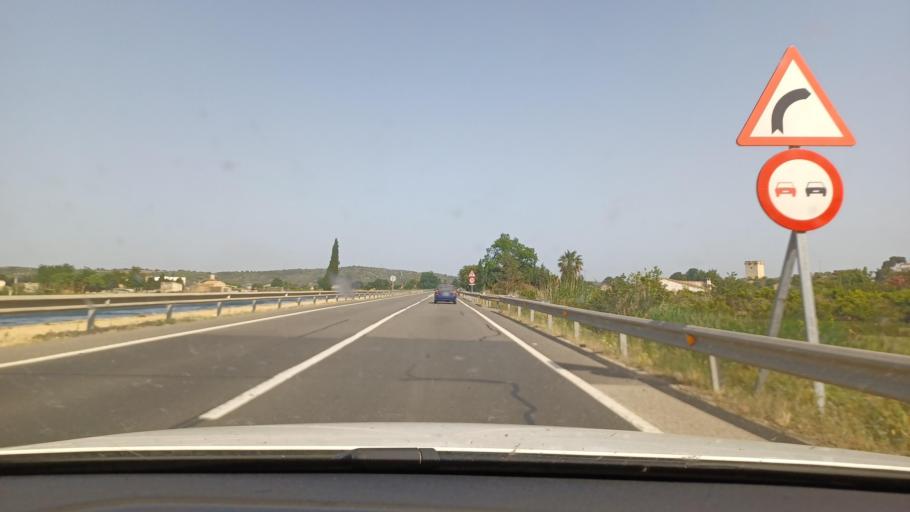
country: ES
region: Catalonia
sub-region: Provincia de Tarragona
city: Masdenverge
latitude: 40.7480
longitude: 0.5556
